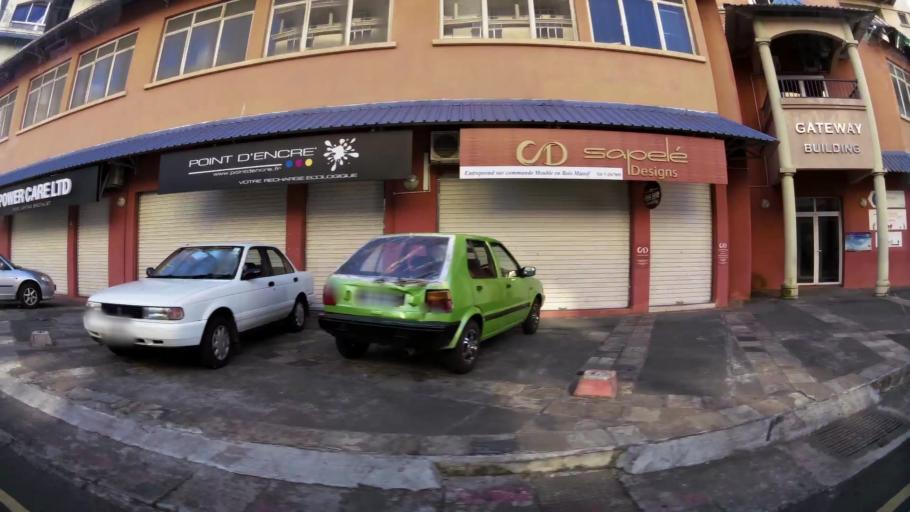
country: MU
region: Plaines Wilhems
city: Quatre Bornes
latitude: -20.2595
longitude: 57.4843
